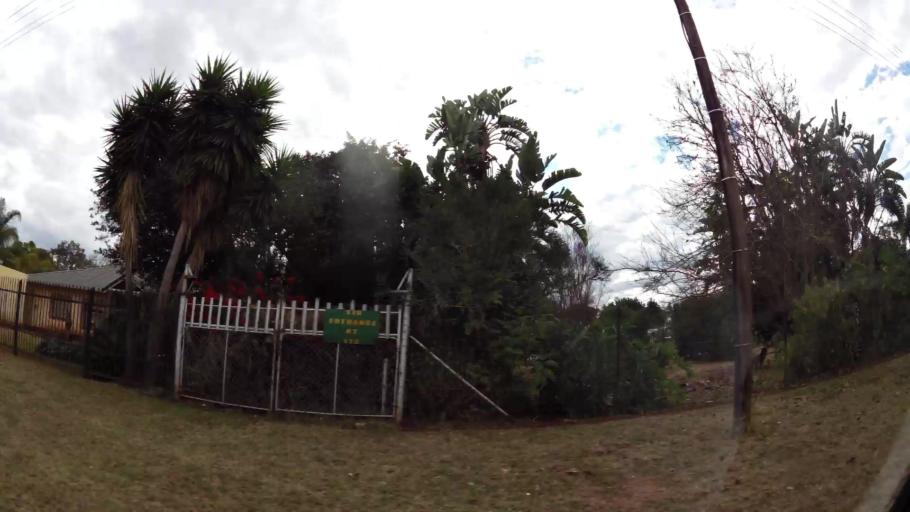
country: ZA
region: Limpopo
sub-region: Waterberg District Municipality
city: Modimolle
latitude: -24.5104
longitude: 28.7154
